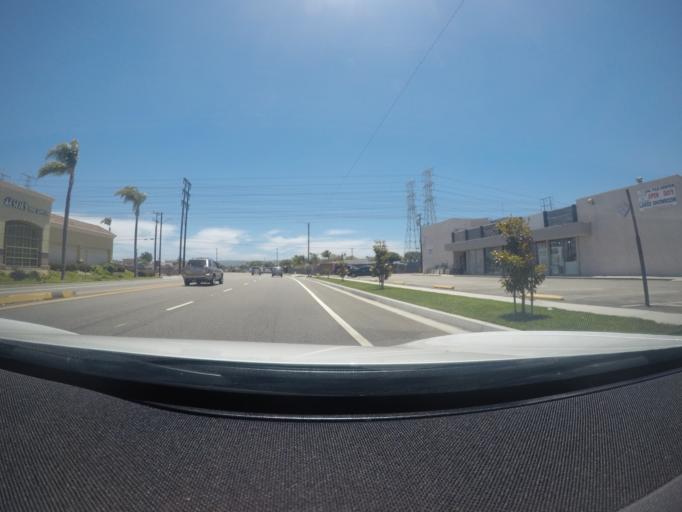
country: US
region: California
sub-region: Los Angeles County
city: Redondo Beach
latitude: 33.8568
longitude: -118.3655
